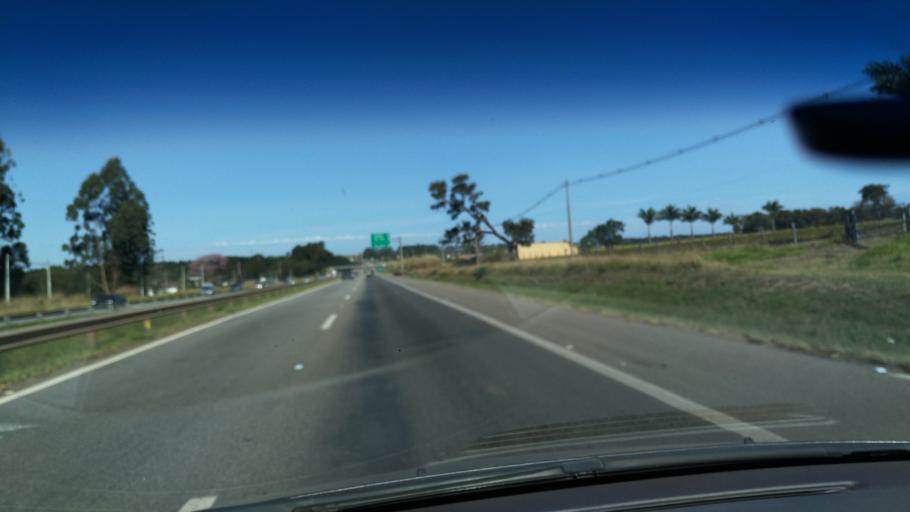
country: BR
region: Sao Paulo
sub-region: Santo Antonio De Posse
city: Santo Antonio de Posse
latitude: -22.6129
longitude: -47.0073
